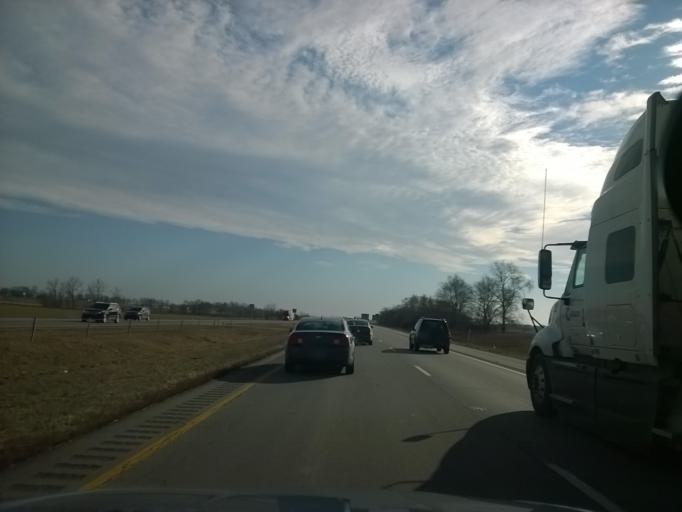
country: US
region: Indiana
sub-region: Johnson County
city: Edinburgh
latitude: 39.3729
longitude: -85.9428
